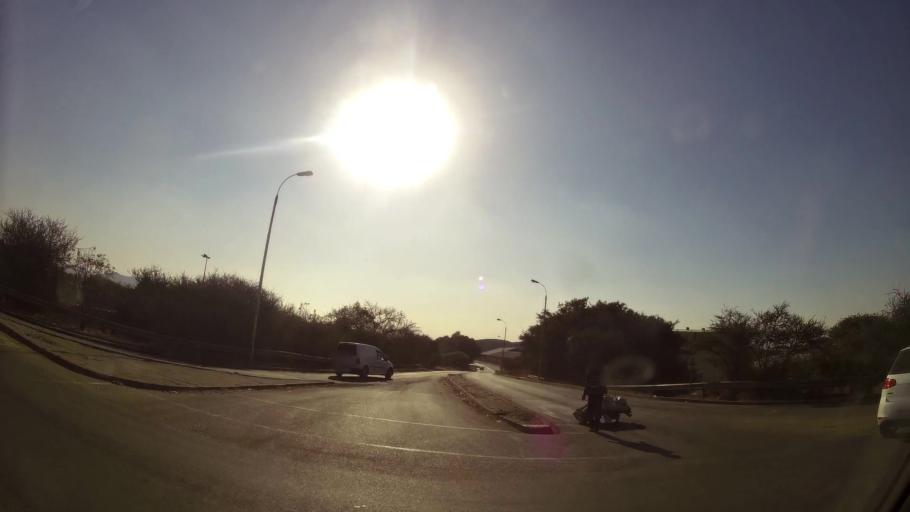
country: ZA
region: North-West
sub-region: Bojanala Platinum District Municipality
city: Rustenburg
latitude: -25.6698
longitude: 27.2558
